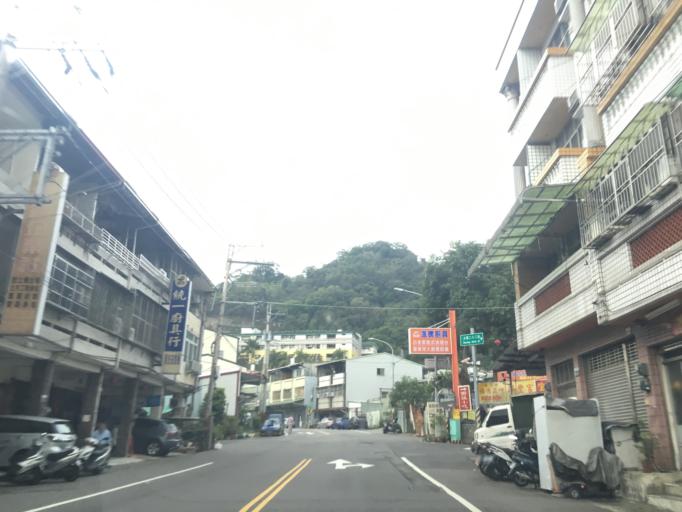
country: TW
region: Taiwan
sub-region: Taichung City
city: Taichung
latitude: 24.1574
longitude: 120.7424
